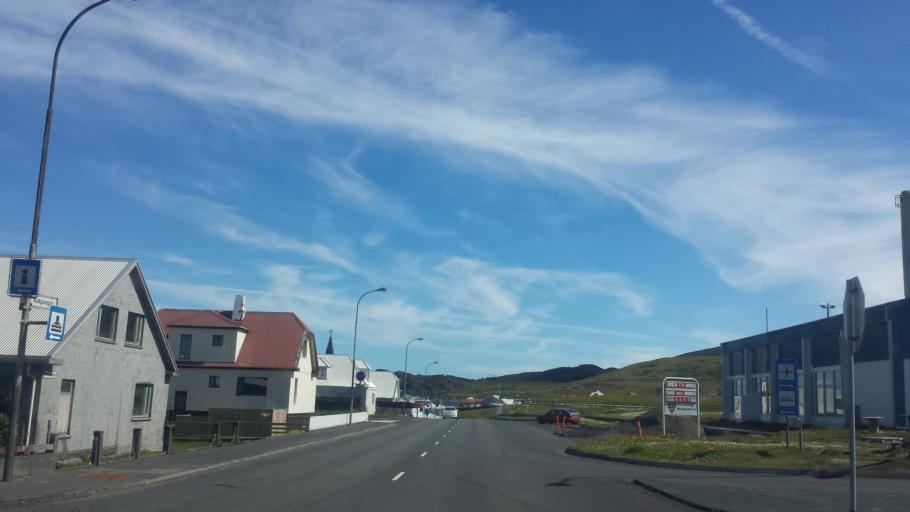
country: IS
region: South
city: Vestmannaeyjar
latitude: 63.4363
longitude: -20.2766
